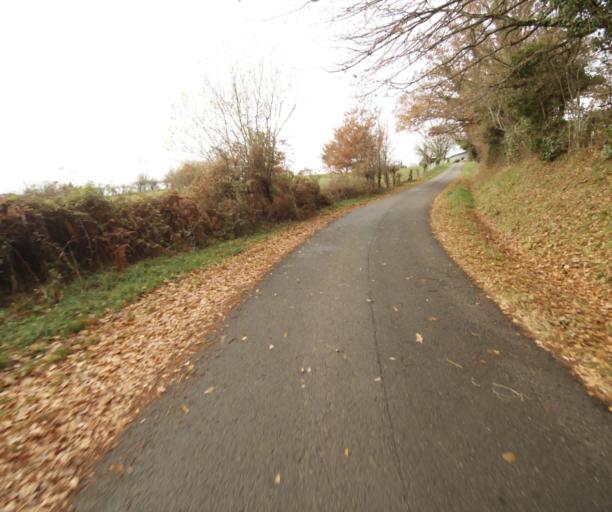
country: FR
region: Limousin
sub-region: Departement de la Correze
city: Sainte-Fereole
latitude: 45.2614
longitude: 1.6060
